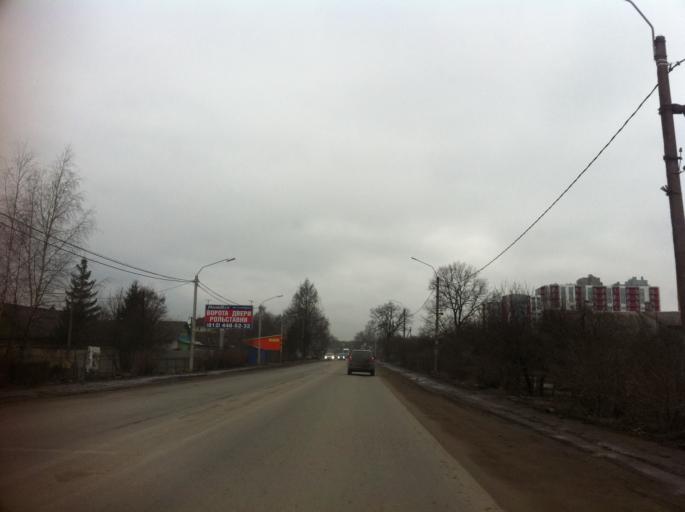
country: RU
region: Leningrad
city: Yanino Vtoroye
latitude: 59.9463
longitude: 30.5690
